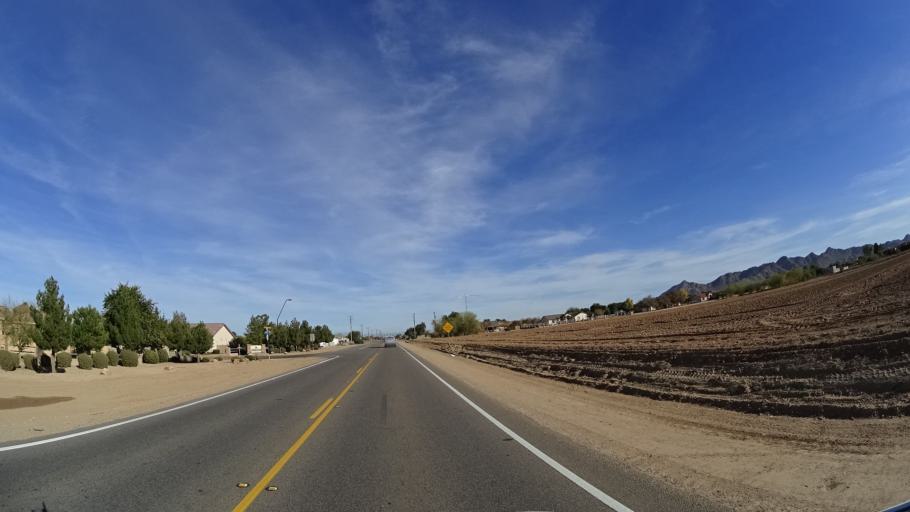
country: US
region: Arizona
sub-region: Maricopa County
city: Queen Creek
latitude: 33.2195
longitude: -111.6752
